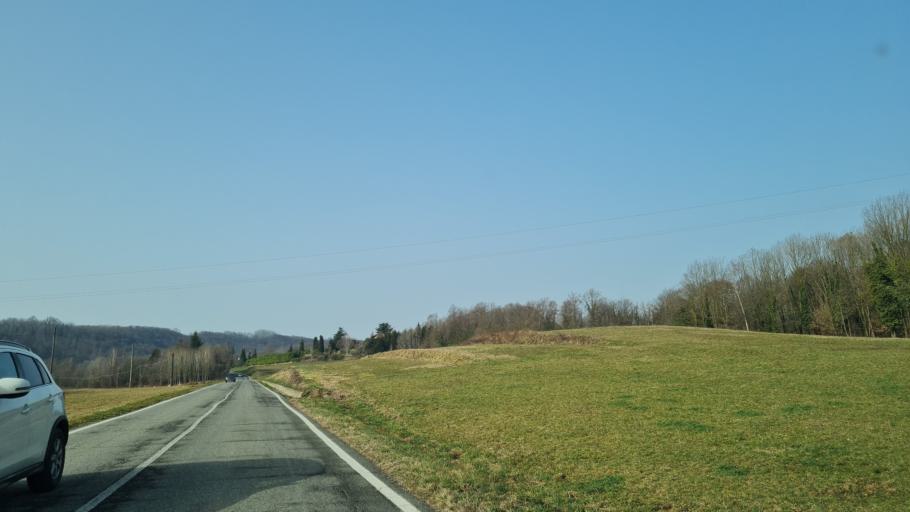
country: IT
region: Piedmont
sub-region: Provincia di Biella
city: Zimone
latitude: 45.4586
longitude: 8.0473
